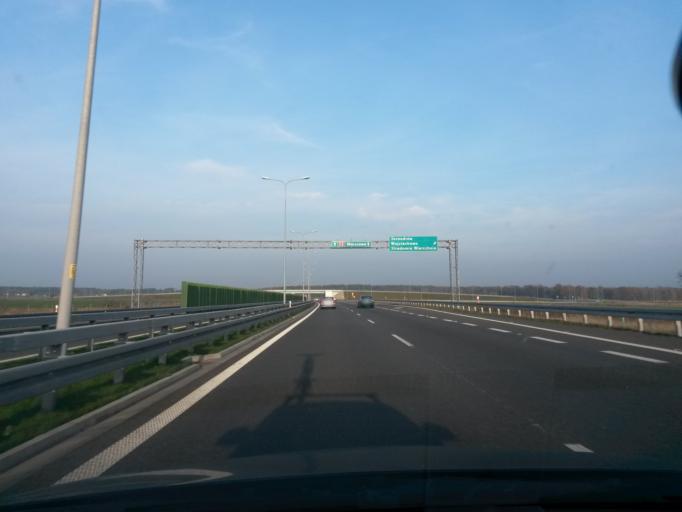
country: PL
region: Lower Silesian Voivodeship
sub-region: Powiat olesnicki
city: Twardogora
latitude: 51.2823
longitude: 17.5702
